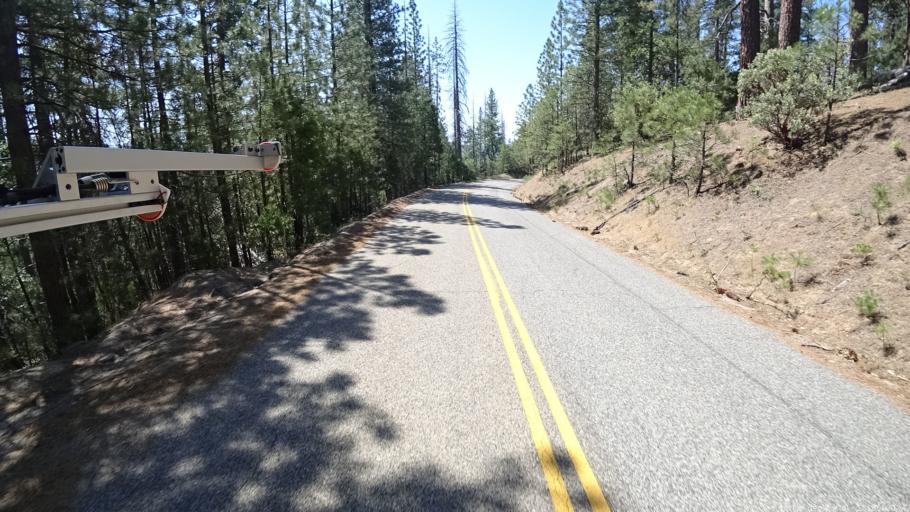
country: US
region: California
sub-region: Madera County
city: Oakhurst
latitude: 37.3960
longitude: -119.3516
